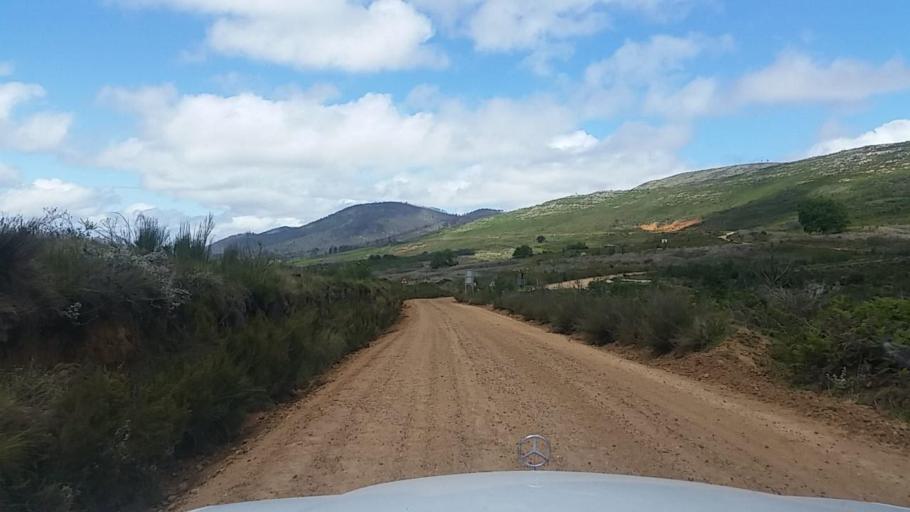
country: ZA
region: Western Cape
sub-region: Eden District Municipality
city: Knysna
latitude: -33.8817
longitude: 23.1570
